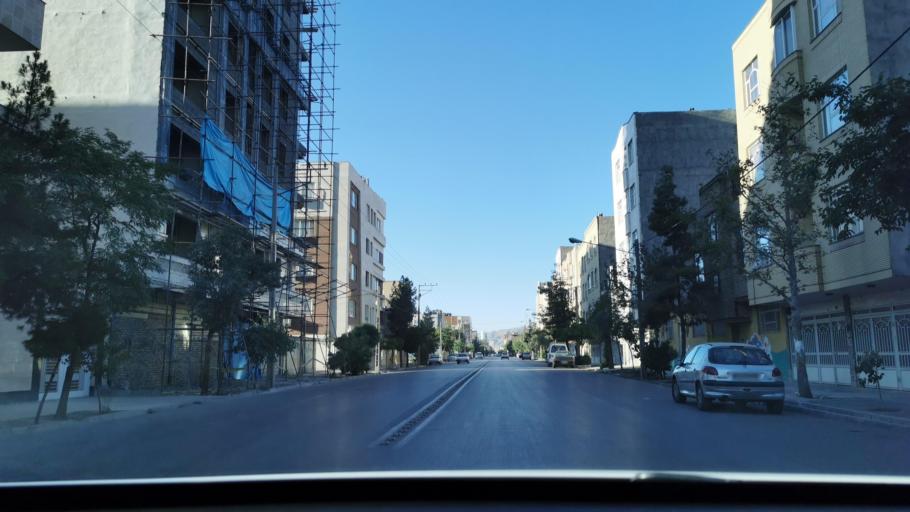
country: IR
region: Razavi Khorasan
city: Mashhad
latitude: 36.3566
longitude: 59.4972
